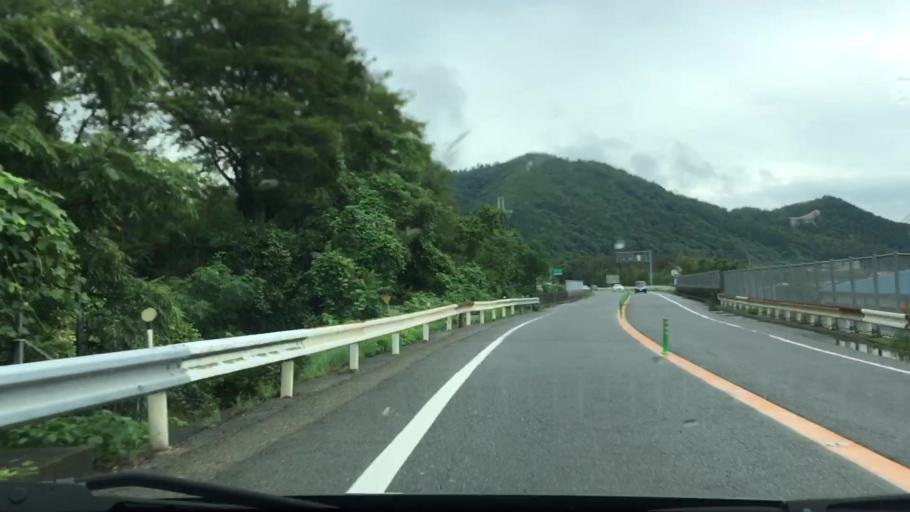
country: JP
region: Hyogo
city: Himeji
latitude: 35.0075
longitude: 134.7642
